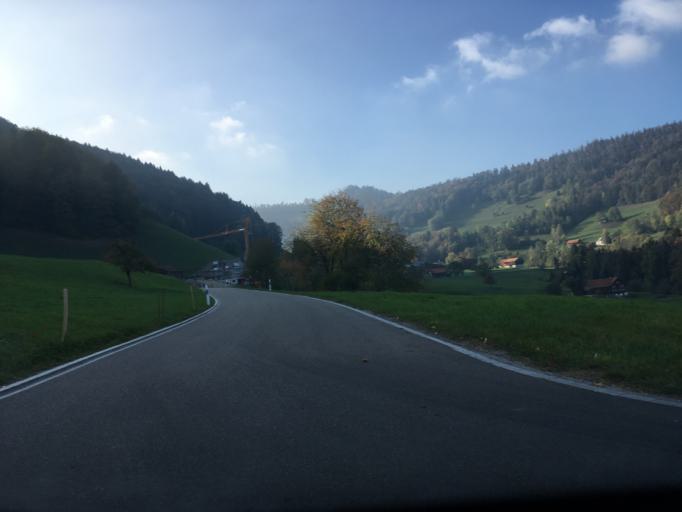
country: CH
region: Saint Gallen
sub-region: Wahlkreis Toggenburg
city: Mosnang
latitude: 47.3423
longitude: 9.0437
